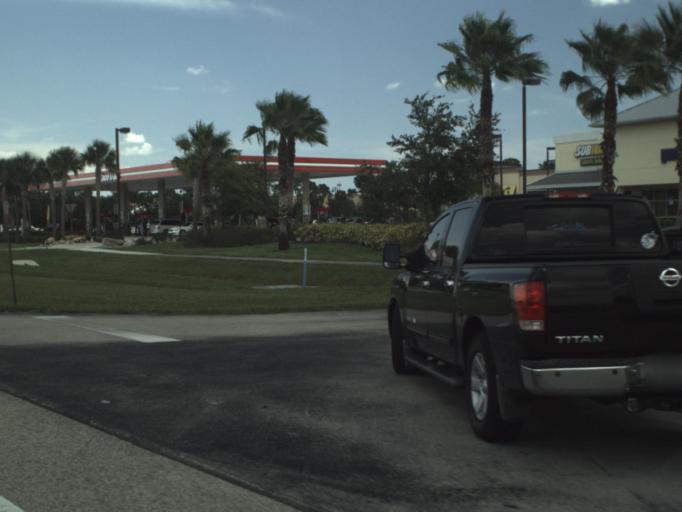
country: US
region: Florida
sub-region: Martin County
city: Port Salerno
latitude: 27.1536
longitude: -80.2193
